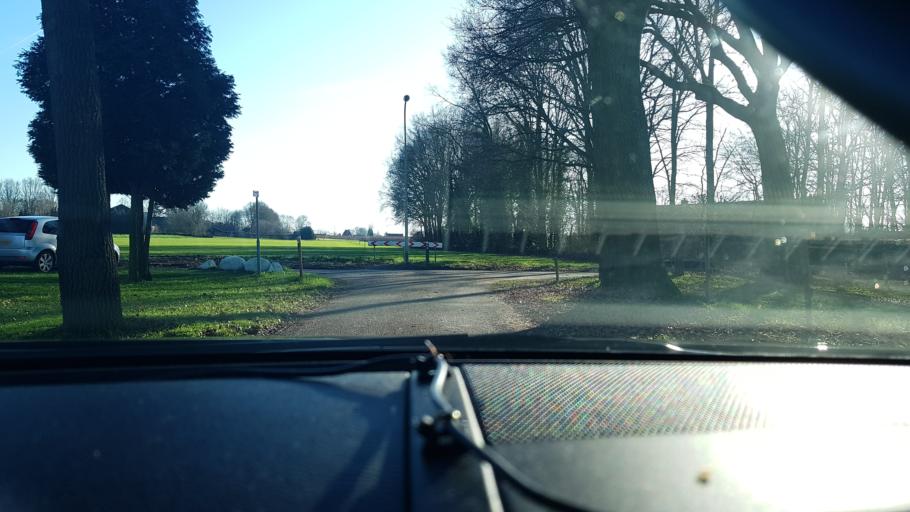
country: NL
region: Limburg
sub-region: Gemeente Leudal
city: Haelen
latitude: 51.2709
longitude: 5.9891
